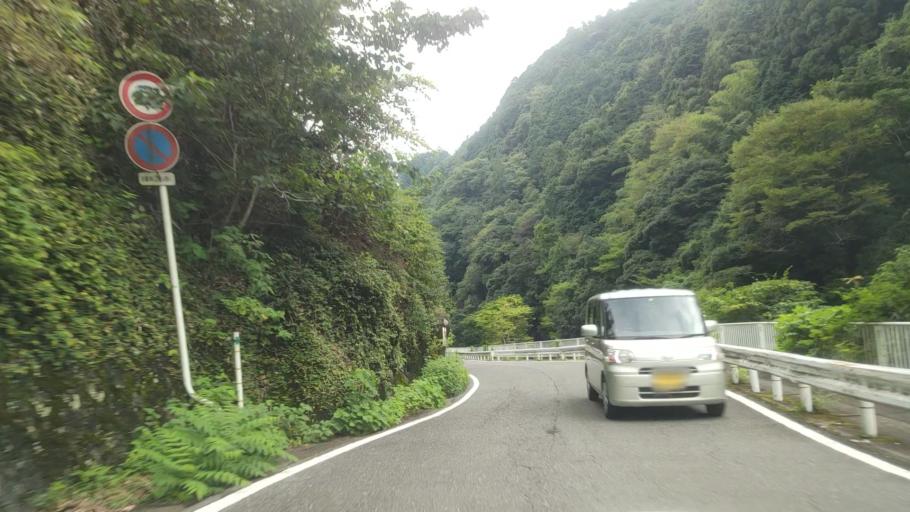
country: JP
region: Wakayama
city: Hashimoto
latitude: 34.2793
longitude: 135.5635
